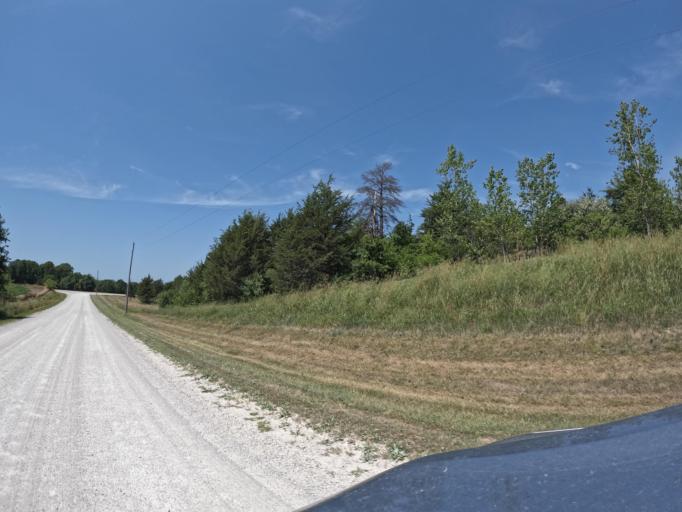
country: US
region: Iowa
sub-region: Henry County
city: Mount Pleasant
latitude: 40.9300
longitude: -91.6203
